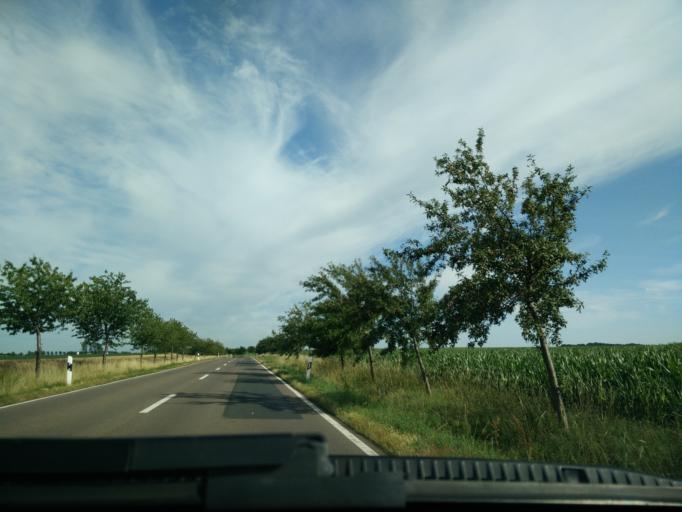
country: DE
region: Saxony
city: Bad Lausick
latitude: 51.1174
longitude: 12.6735
